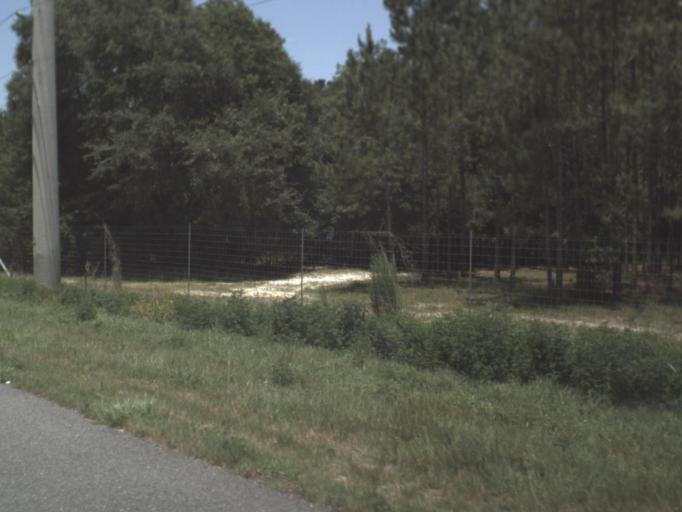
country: US
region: Florida
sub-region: Levy County
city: Manatee Road
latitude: 29.6165
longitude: -82.9830
